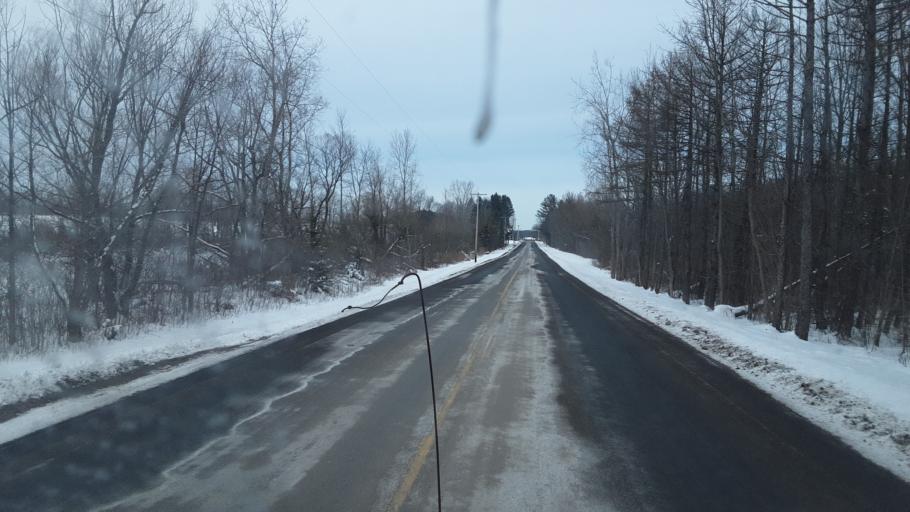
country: US
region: New York
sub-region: Wayne County
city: Lyons
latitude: 43.1002
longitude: -77.0438
